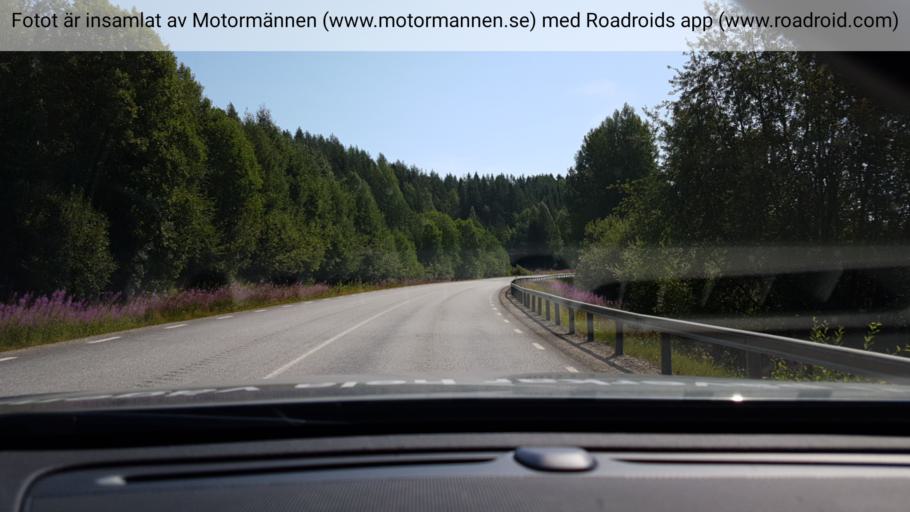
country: SE
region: Vaesterbotten
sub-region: Vindelns Kommun
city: Vindeln
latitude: 64.3119
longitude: 19.6053
